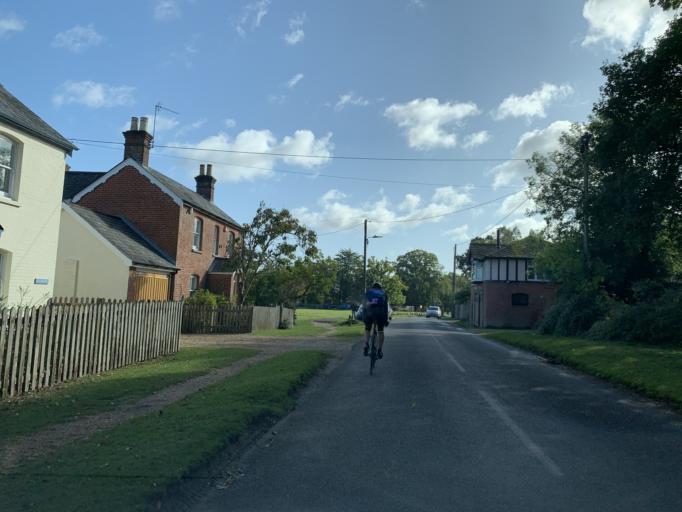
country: GB
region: England
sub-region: Hampshire
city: Brockenhurst
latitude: 50.8225
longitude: -1.5839
